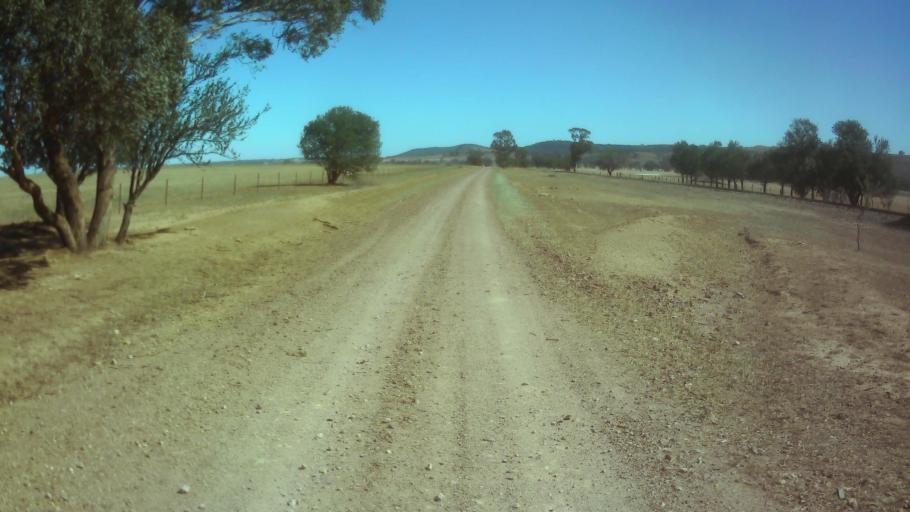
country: AU
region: New South Wales
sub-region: Weddin
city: Grenfell
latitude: -33.9597
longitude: 148.3039
